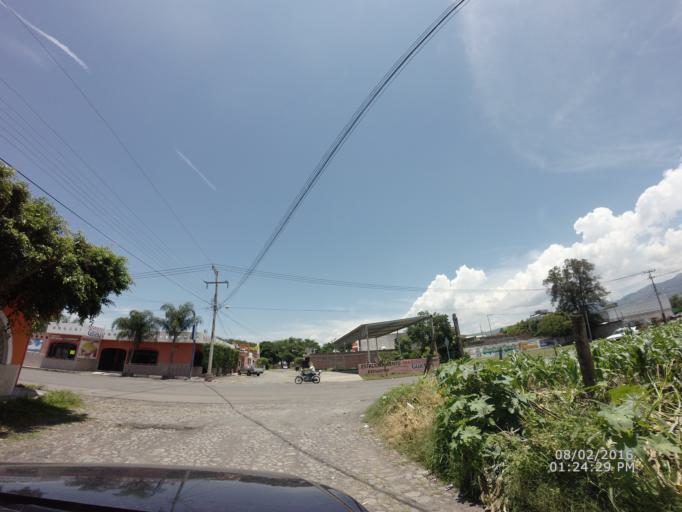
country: MX
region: Nayarit
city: Ixtlan del Rio
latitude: 21.0388
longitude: -104.3773
